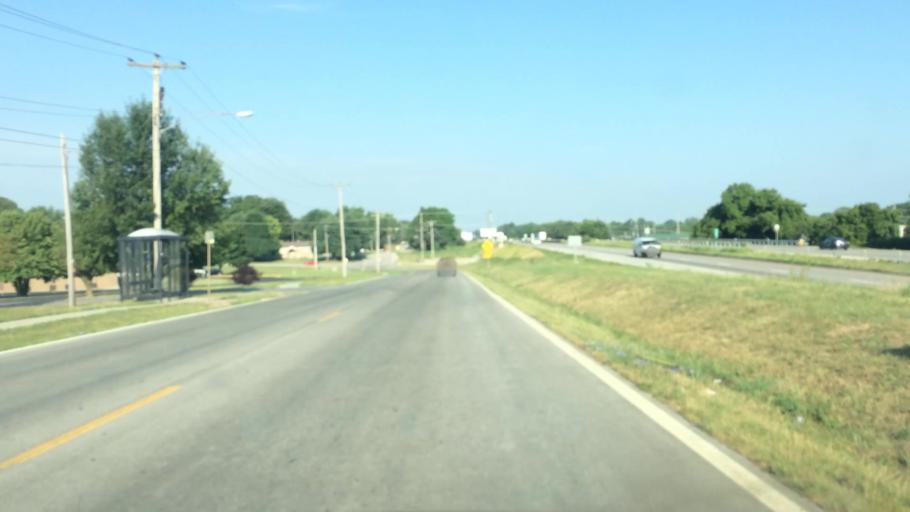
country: US
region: Missouri
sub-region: Greene County
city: Springfield
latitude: 37.2500
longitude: -93.2717
